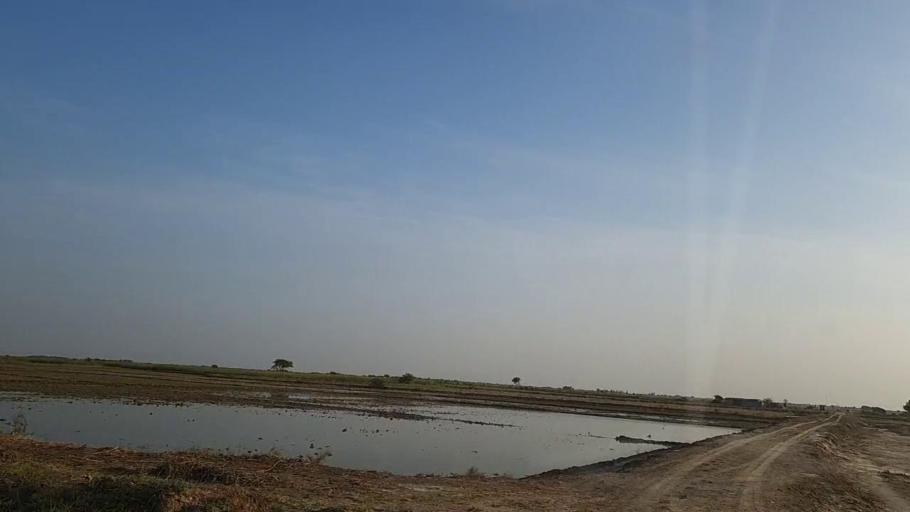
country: PK
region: Sindh
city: Mirpur Batoro
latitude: 24.6078
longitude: 68.1025
